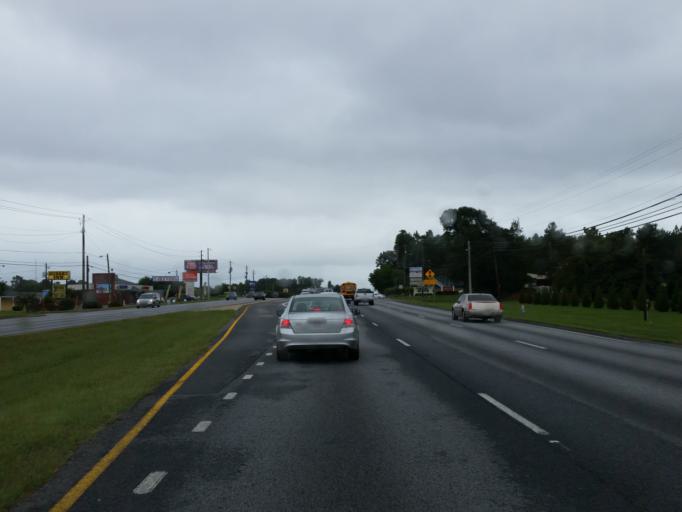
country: US
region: Georgia
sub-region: Clayton County
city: Morrow
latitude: 33.5675
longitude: -84.3717
